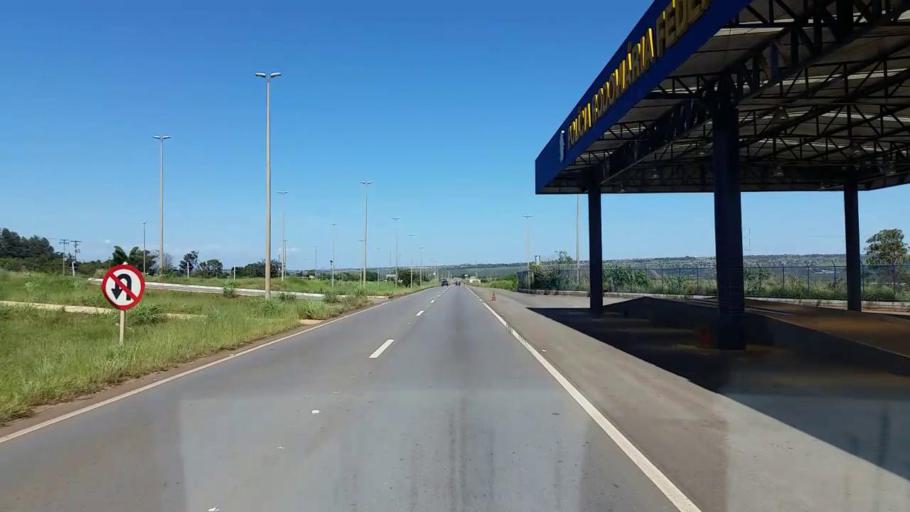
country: BR
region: Federal District
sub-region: Brasilia
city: Brasilia
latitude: -15.7949
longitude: -48.1984
